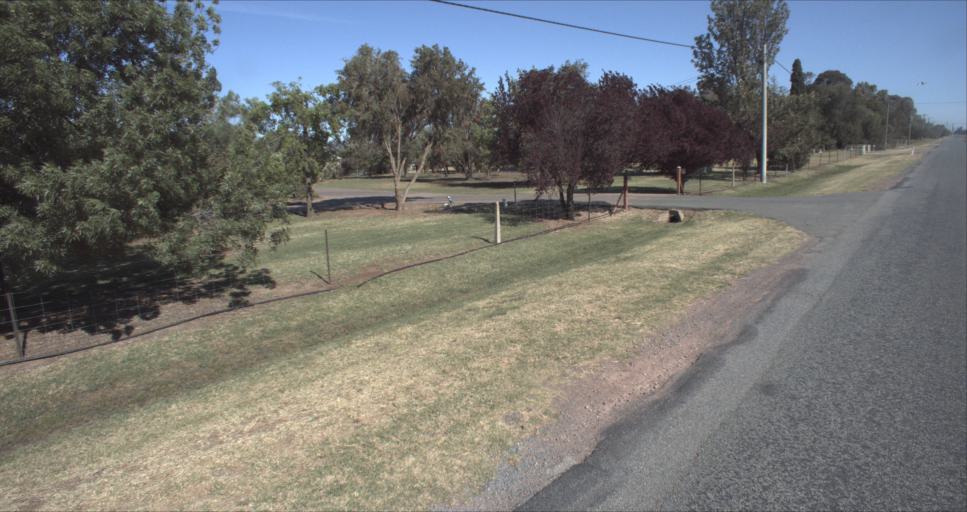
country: AU
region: New South Wales
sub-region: Leeton
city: Leeton
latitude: -34.5382
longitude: 146.4196
